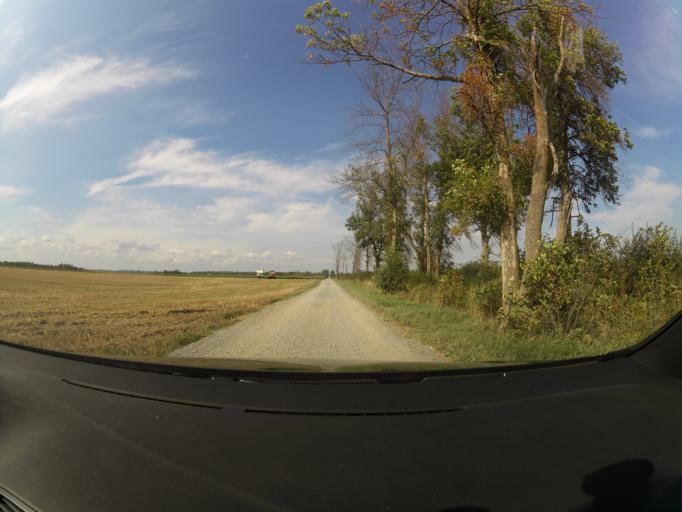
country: CA
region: Ontario
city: Carleton Place
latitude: 45.2862
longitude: -76.2149
